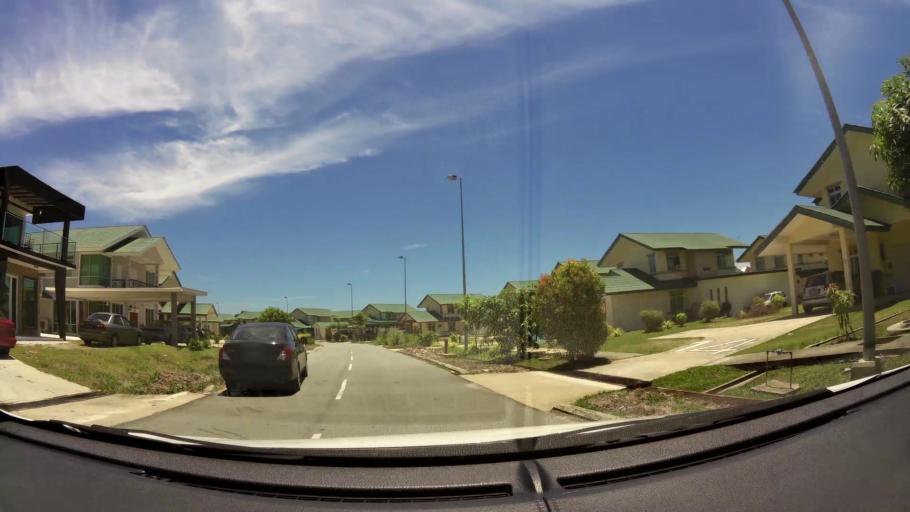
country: BN
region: Brunei and Muara
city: Bandar Seri Begawan
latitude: 5.0224
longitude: 115.0351
